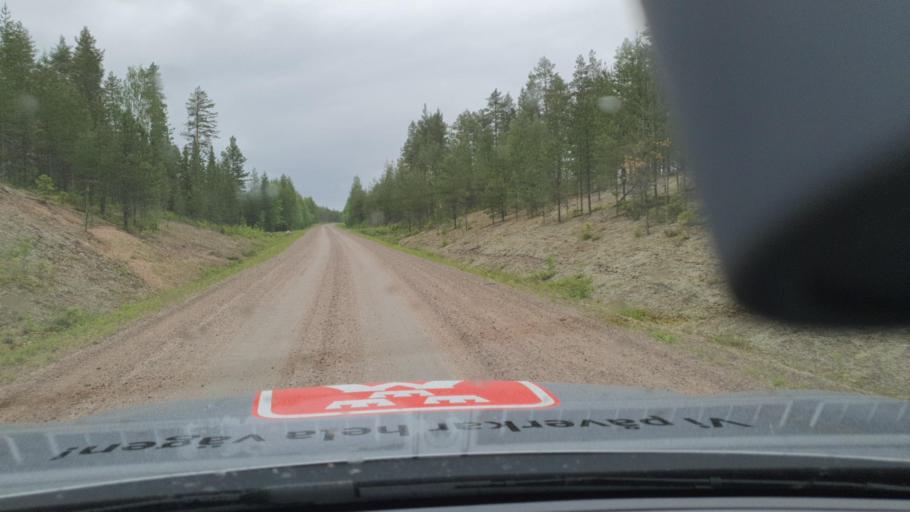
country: SE
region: Norrbotten
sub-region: Overkalix Kommun
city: OEverkalix
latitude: 66.5682
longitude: 22.7496
